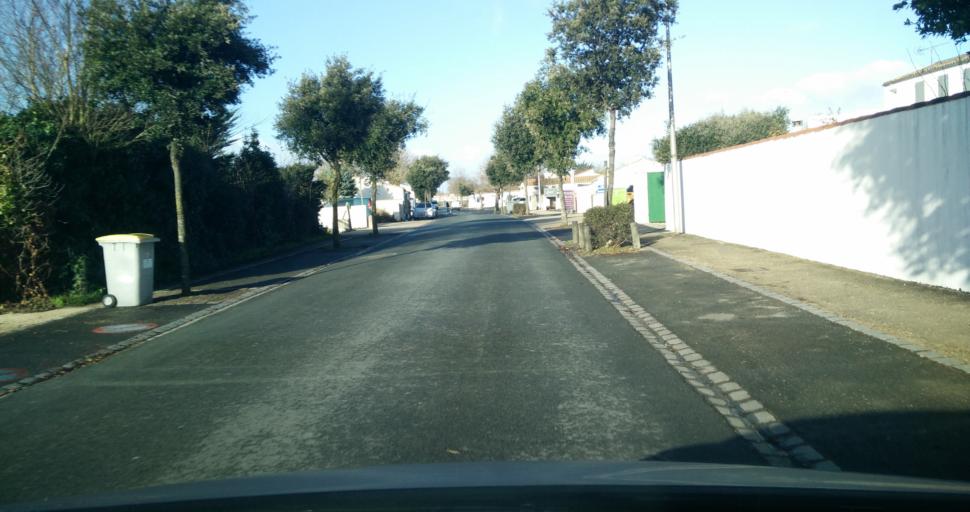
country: FR
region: Poitou-Charentes
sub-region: Departement de la Charente-Maritime
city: Saint-Martin-de-Re
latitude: 46.1977
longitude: -1.3575
